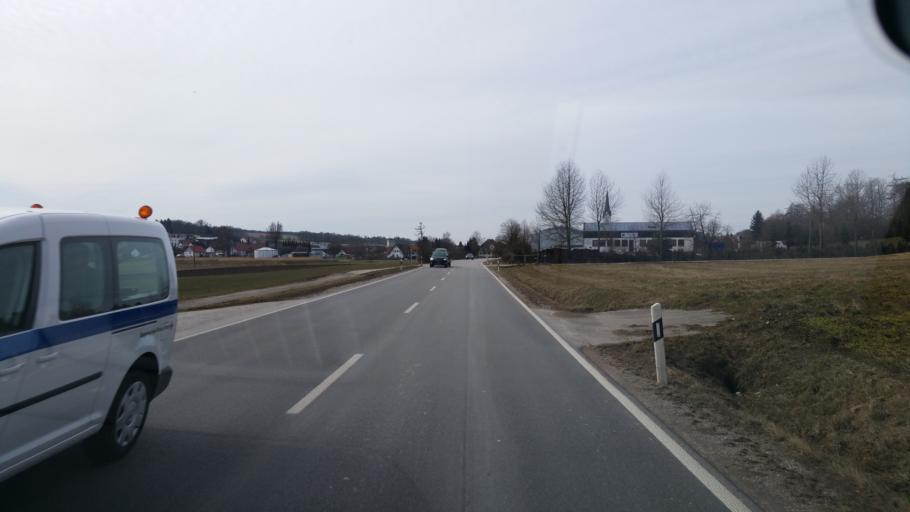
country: DE
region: Bavaria
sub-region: Lower Bavaria
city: Furth
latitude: 48.5902
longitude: 12.0321
